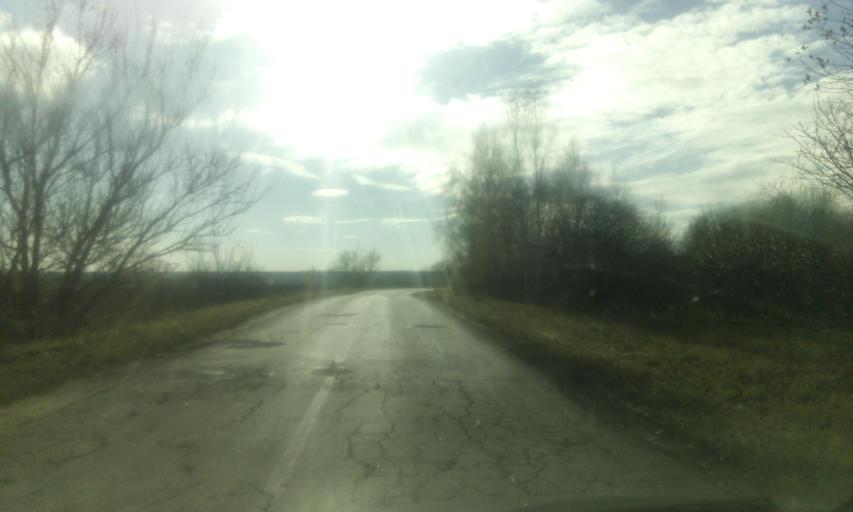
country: RU
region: Tula
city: Dubovka
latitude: 53.9589
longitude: 38.0417
